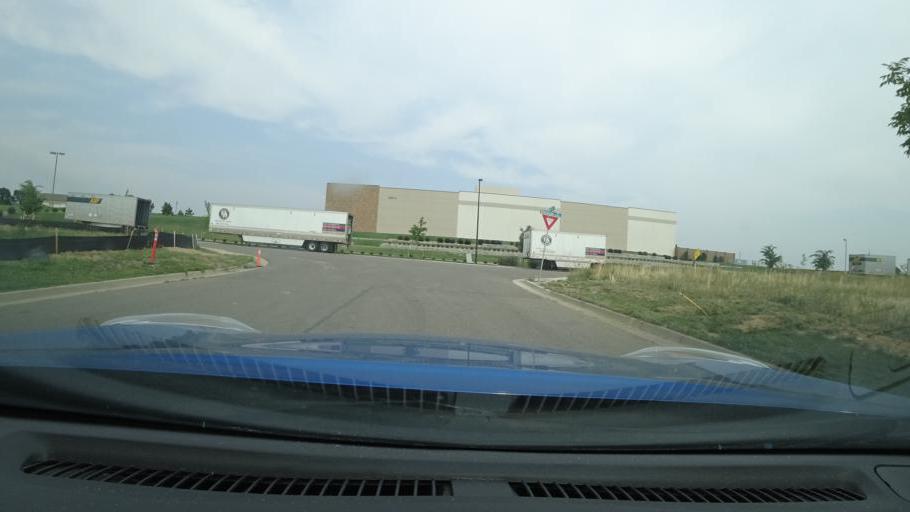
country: US
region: Colorado
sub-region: Adams County
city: Aurora
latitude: 39.7488
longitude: -104.7539
